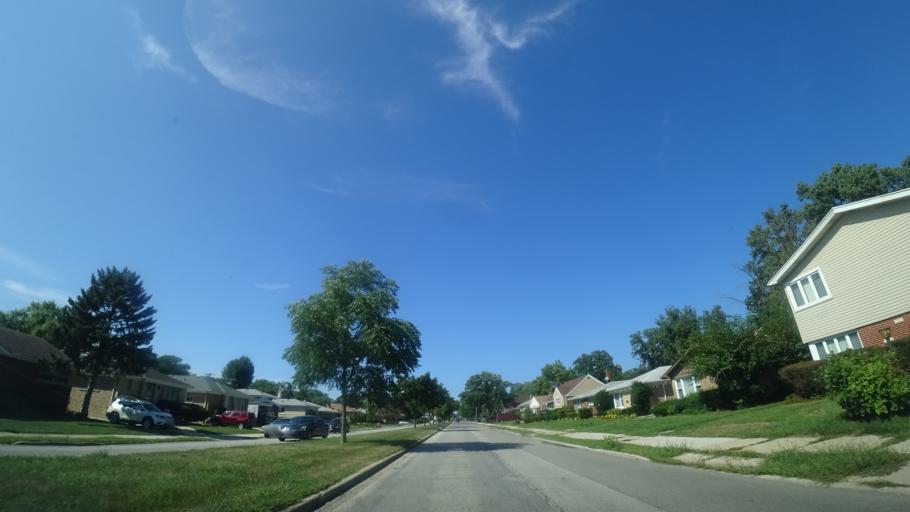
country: US
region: Illinois
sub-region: Cook County
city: Skokie
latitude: 42.0373
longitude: -87.7278
